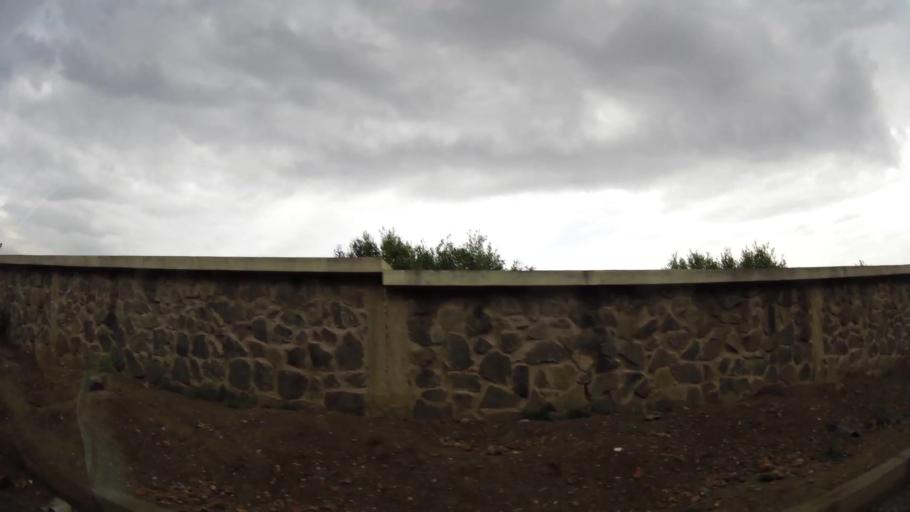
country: MA
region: Oriental
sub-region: Nador
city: Nador
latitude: 35.1472
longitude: -2.9795
